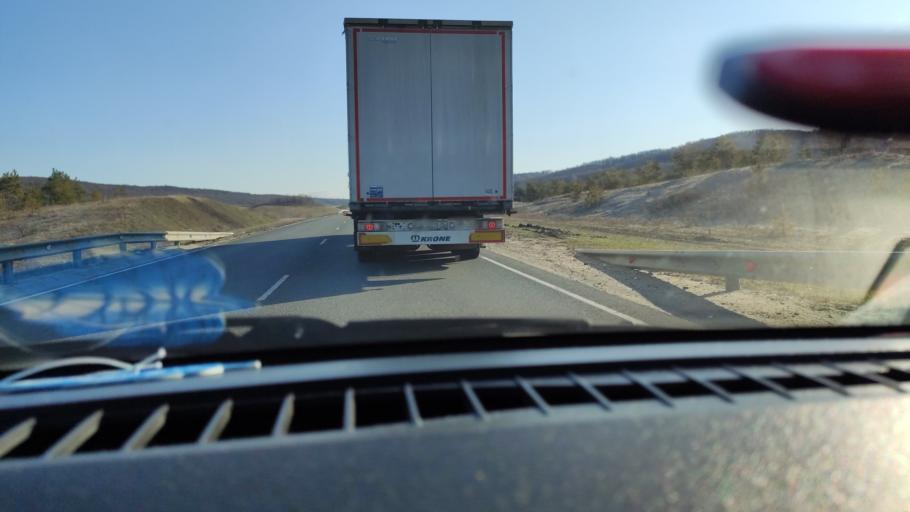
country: RU
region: Saratov
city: Alekseyevka
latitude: 52.3971
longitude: 47.9846
